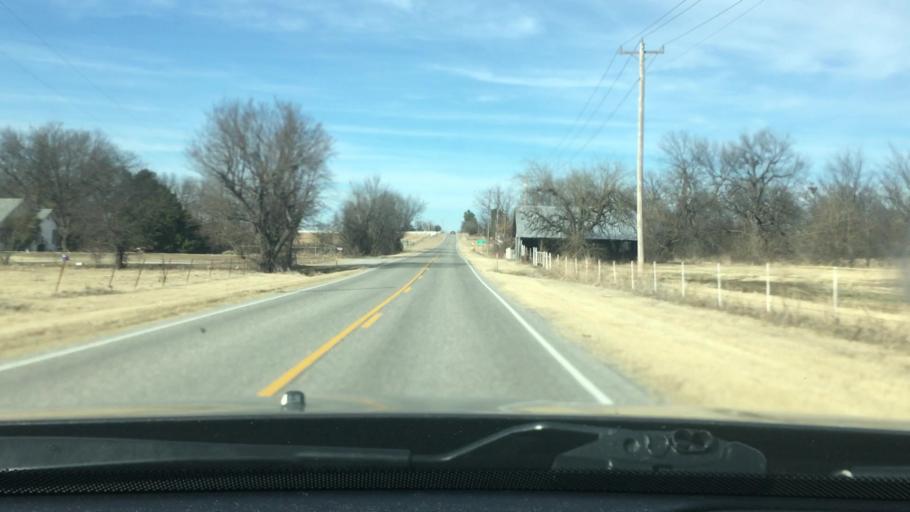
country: US
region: Oklahoma
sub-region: Murray County
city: Davis
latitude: 34.4897
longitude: -97.0905
